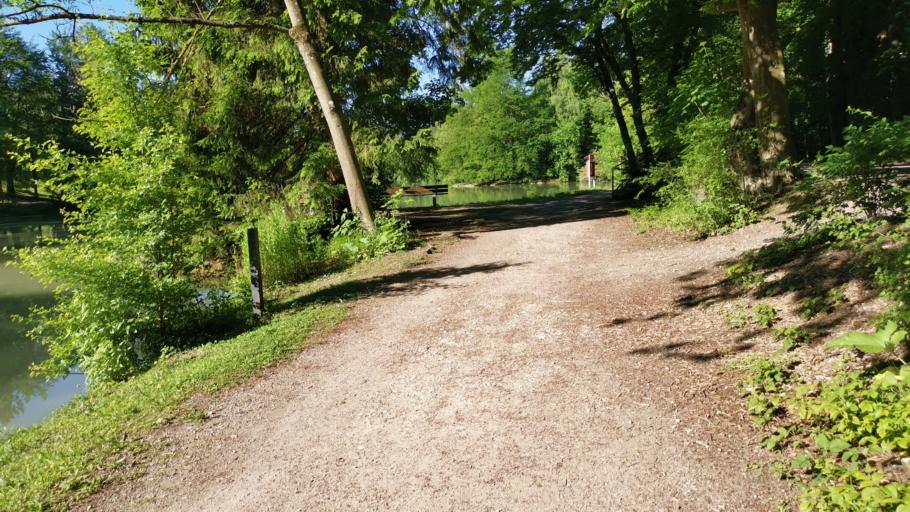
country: DE
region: Bavaria
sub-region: Upper Bavaria
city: Pullach im Isartal
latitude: 48.0870
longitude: 11.5434
